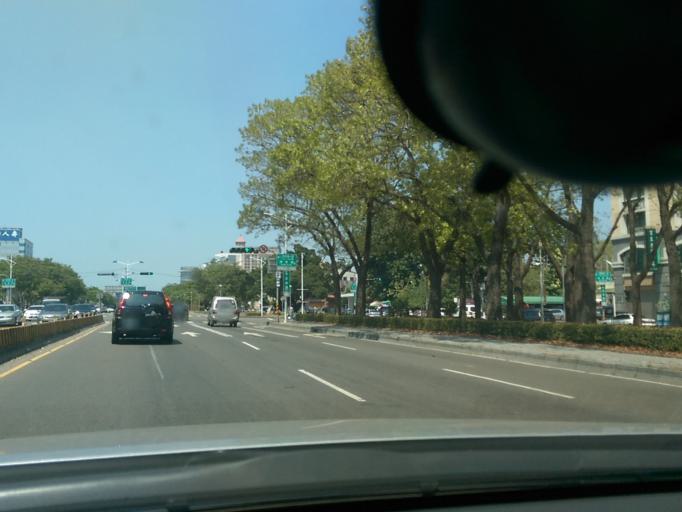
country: TW
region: Taiwan
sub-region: Chiayi
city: Jiayi Shi
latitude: 23.4895
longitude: 120.4530
